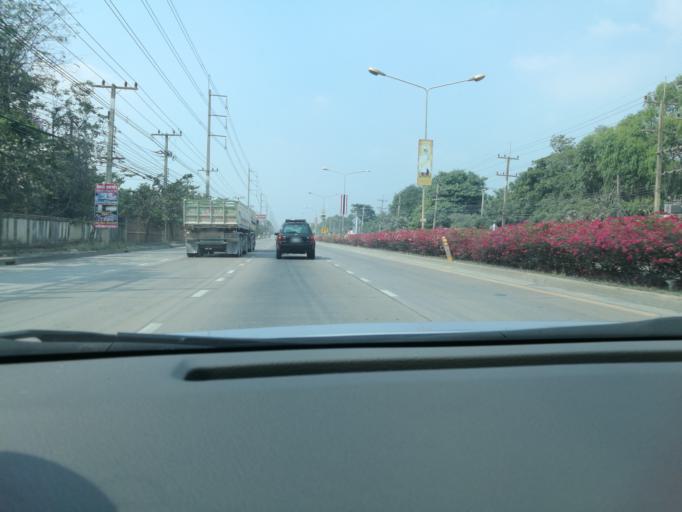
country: TH
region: Sara Buri
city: Phra Phutthabat
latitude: 14.7009
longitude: 100.8569
